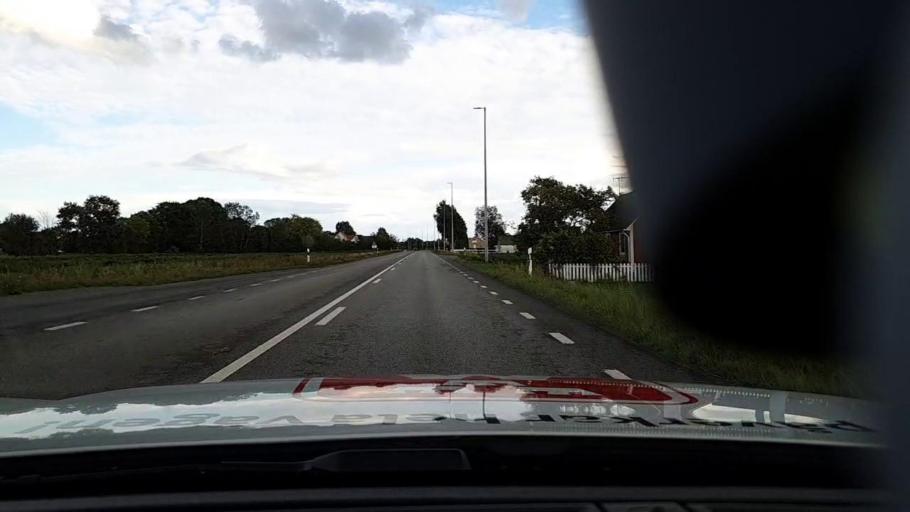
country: SE
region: Blekinge
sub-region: Solvesborgs Kommun
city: Soelvesborg
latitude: 56.0509
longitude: 14.6518
